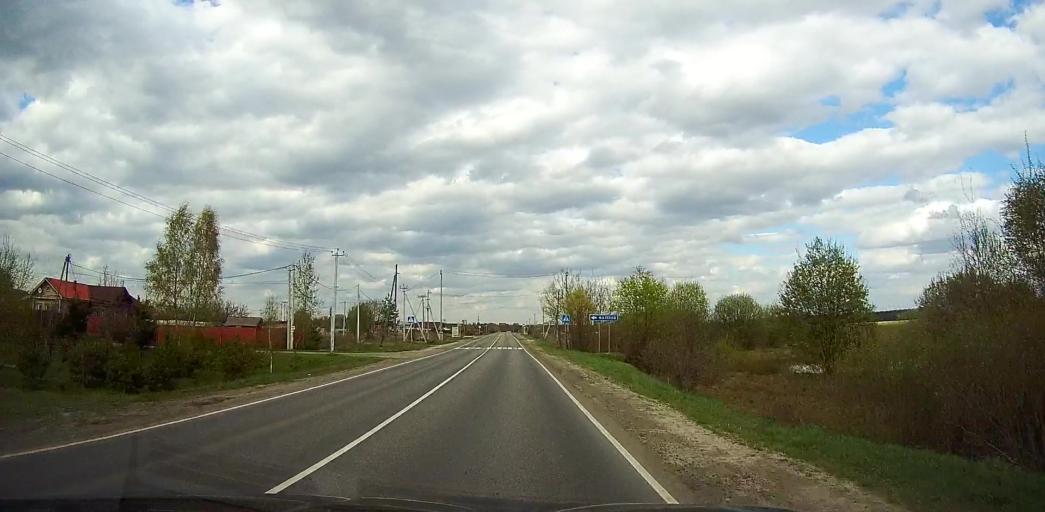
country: RU
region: Moskovskaya
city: Rakhmanovo
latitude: 55.7444
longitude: 38.6486
